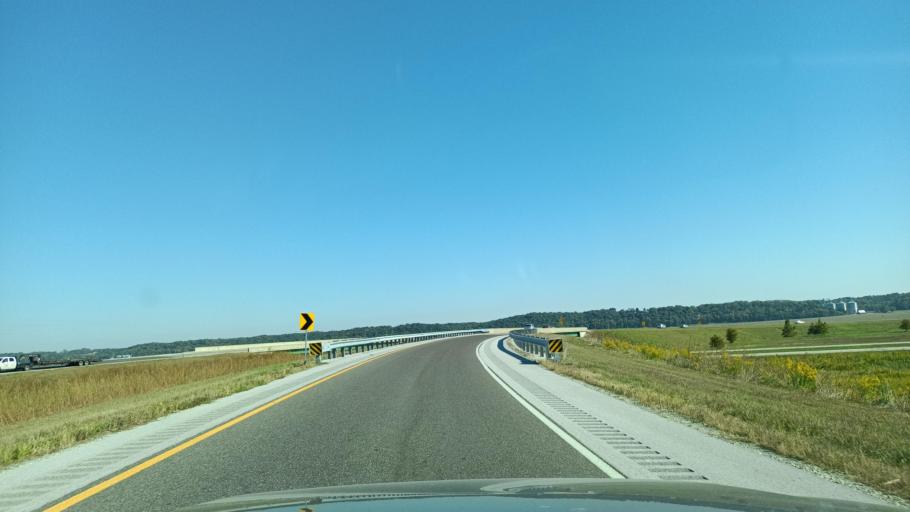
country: US
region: Missouri
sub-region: Marion County
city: Hannibal
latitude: 39.7542
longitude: -91.2992
